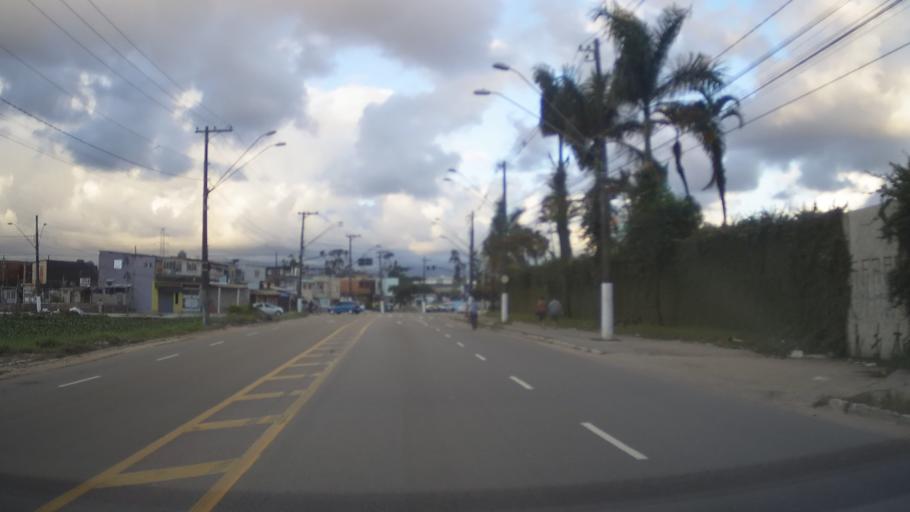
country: BR
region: Sao Paulo
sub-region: Sao Vicente
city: Sao Vicente
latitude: -23.9510
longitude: -46.3909
